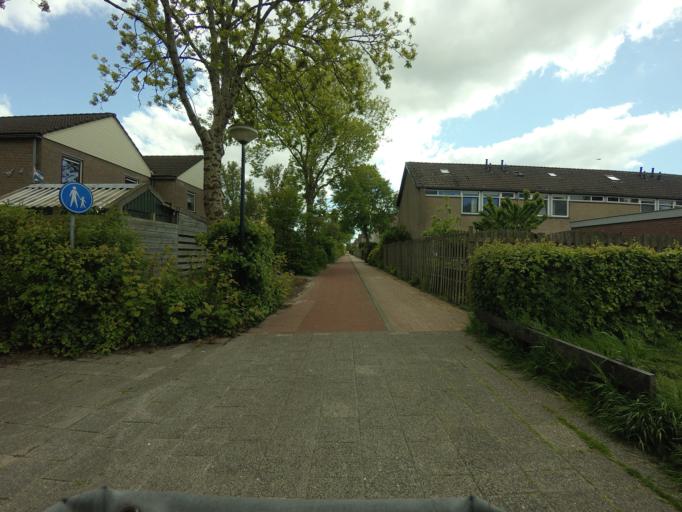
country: NL
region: Friesland
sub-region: Sudwest Fryslan
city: Bolsward
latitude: 53.0711
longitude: 5.5328
